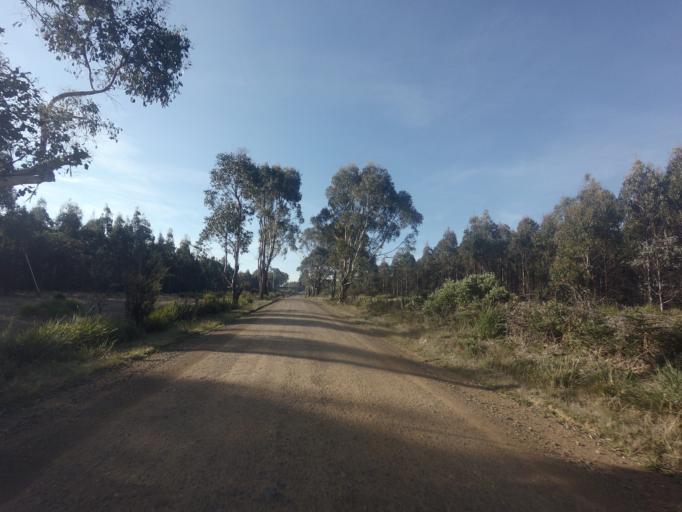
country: AU
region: Tasmania
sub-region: Brighton
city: Bridgewater
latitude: -42.4547
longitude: 147.3821
